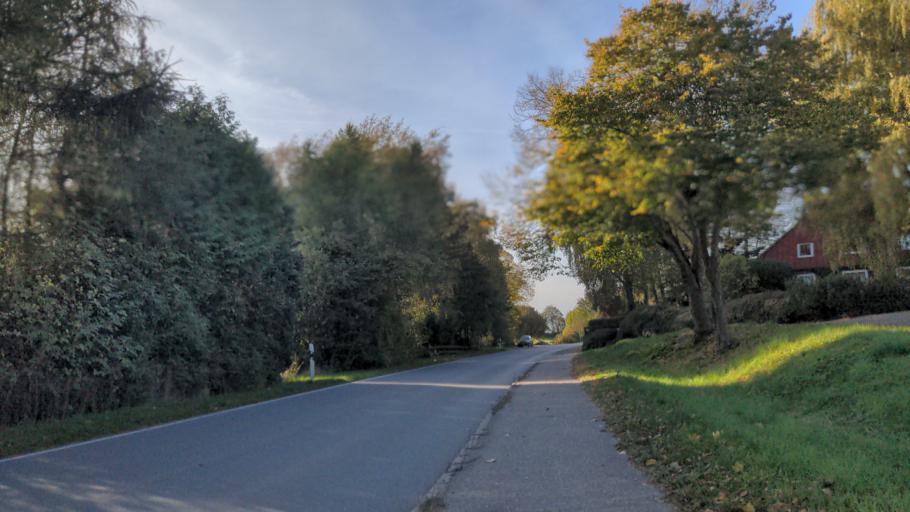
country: DE
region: Schleswig-Holstein
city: Kirchnuchel
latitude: 54.1980
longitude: 10.7009
